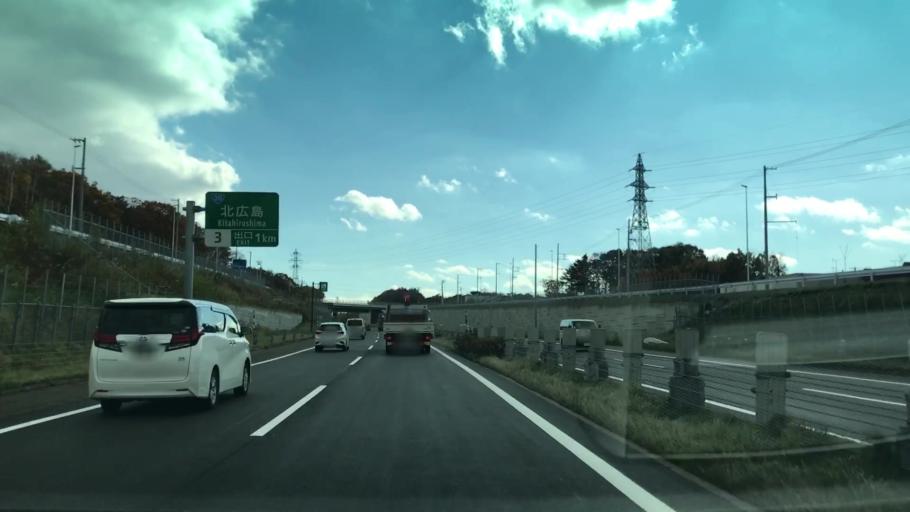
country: JP
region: Hokkaido
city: Kitahiroshima
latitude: 42.9868
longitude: 141.4710
